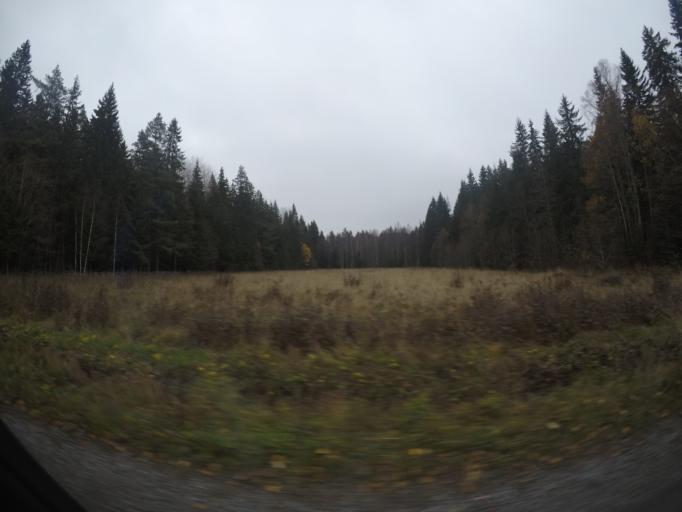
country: SE
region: Vaestmanland
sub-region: Surahammars Kommun
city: Ramnas
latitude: 59.7237
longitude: 16.0946
